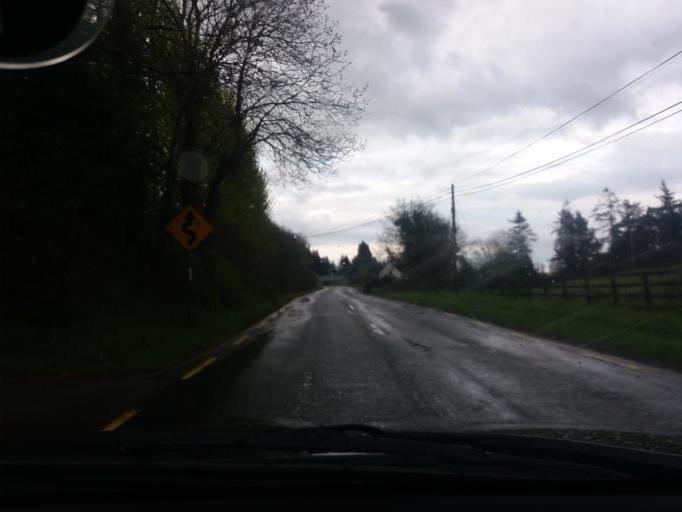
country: IE
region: Ulster
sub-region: An Cabhan
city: Ballyconnell
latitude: 54.1161
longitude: -7.6613
